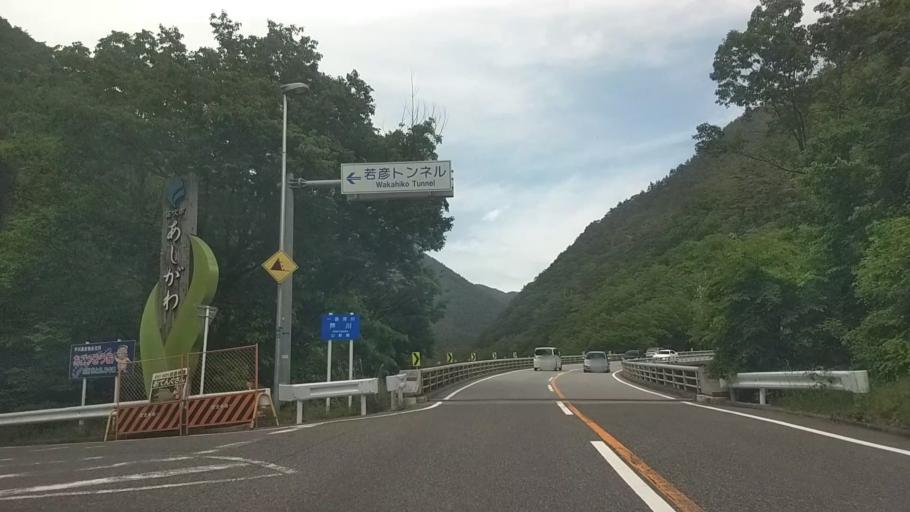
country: JP
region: Yamanashi
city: Fujikawaguchiko
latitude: 35.5306
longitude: 138.6210
